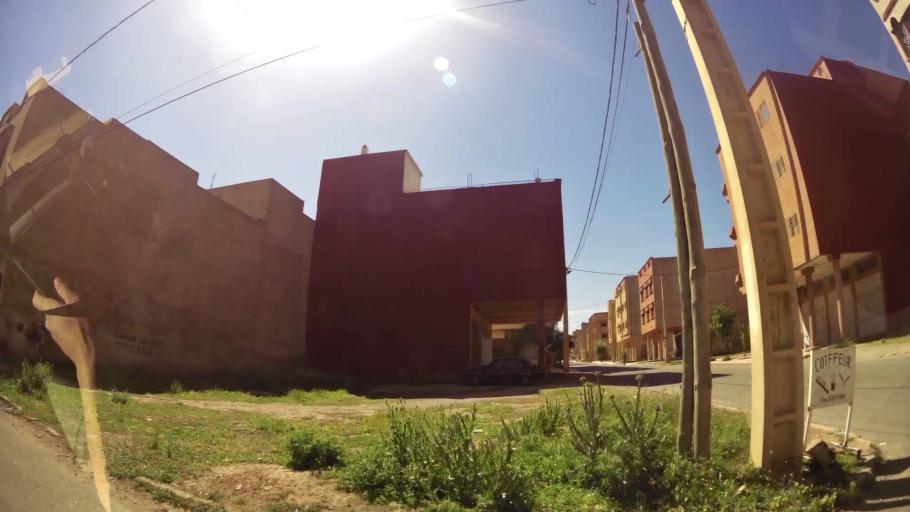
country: MA
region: Oriental
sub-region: Oujda-Angad
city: Oujda
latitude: 34.6576
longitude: -1.8897
